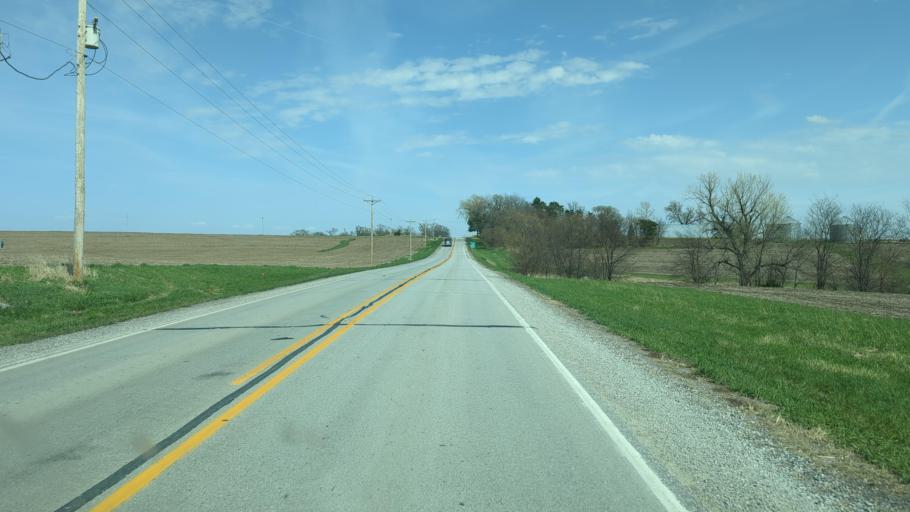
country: US
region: Nebraska
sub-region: Sarpy County
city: Springfield
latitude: 41.0890
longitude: -96.1625
